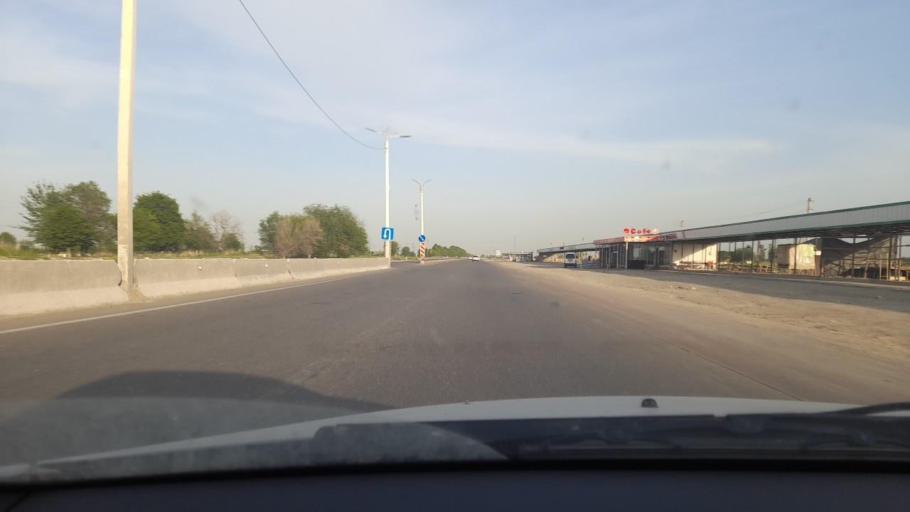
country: KZ
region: Ongtustik Qazaqstan
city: Myrzakent
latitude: 40.5375
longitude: 68.4261
